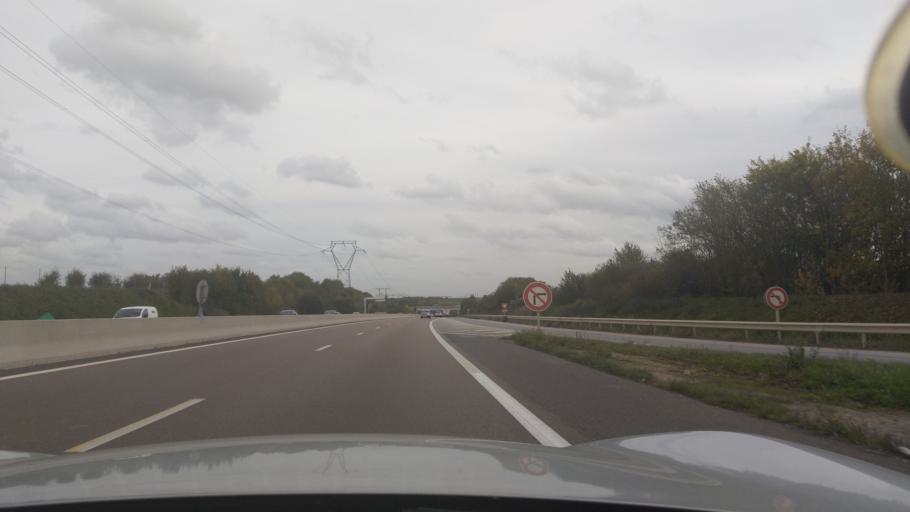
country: FR
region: Ile-de-France
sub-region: Departement du Val-d'Oise
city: Puiseux-en-France
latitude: 49.0419
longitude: 2.4811
